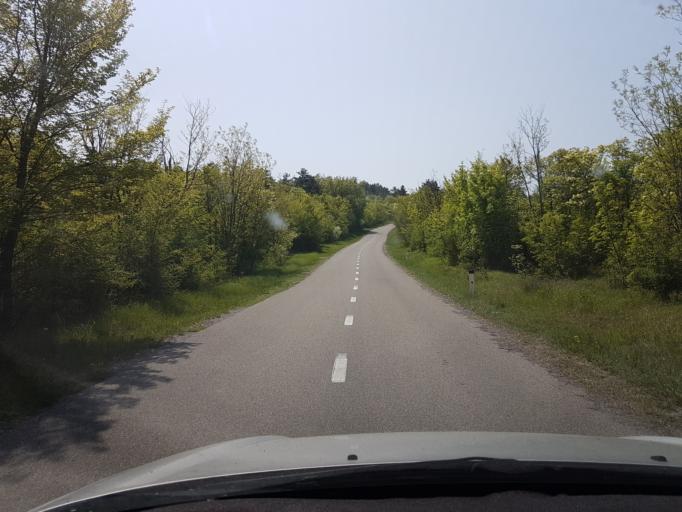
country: SI
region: Komen
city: Komen
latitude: 45.7919
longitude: 13.7073
